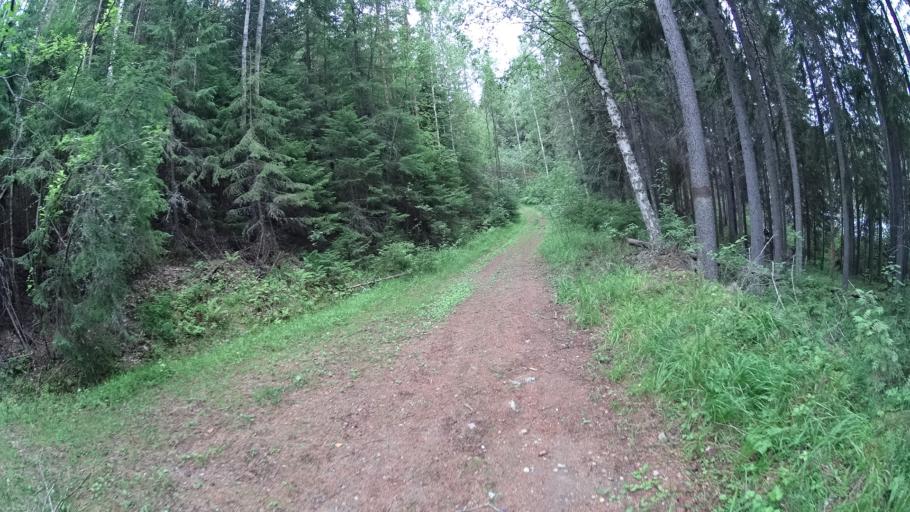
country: FI
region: Southern Savonia
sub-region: Mikkeli
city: Maentyharju
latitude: 61.1761
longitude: 26.8968
